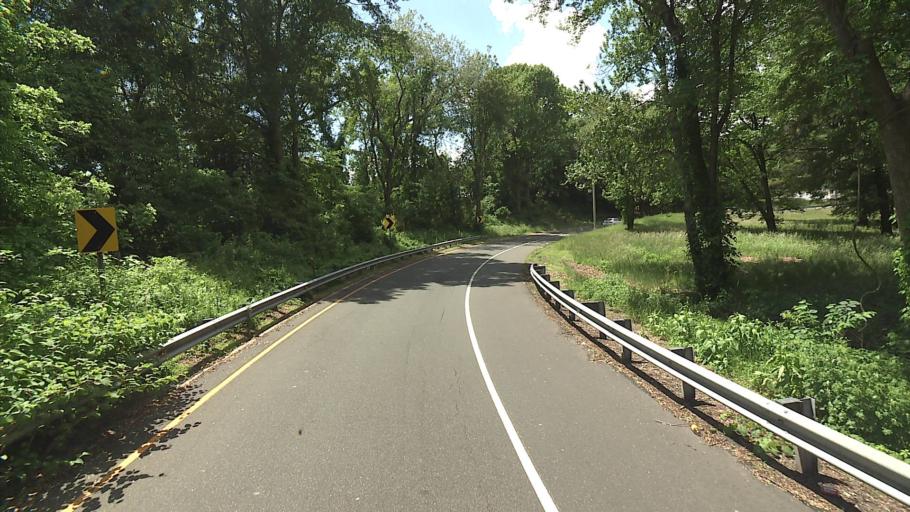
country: US
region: Connecticut
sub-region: New Haven County
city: City of Milford (balance)
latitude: 41.2318
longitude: -73.0688
